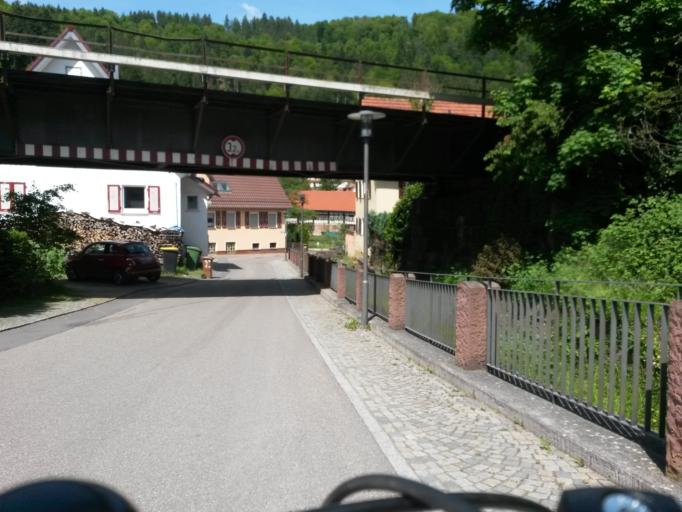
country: DE
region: Baden-Wuerttemberg
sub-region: Karlsruhe Region
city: Bad Liebenzell
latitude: 48.7486
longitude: 8.7333
